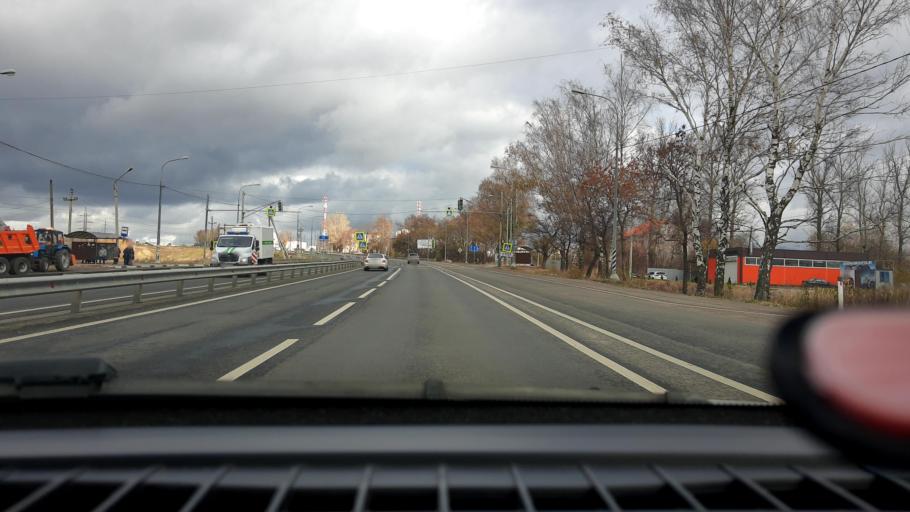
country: RU
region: Nizjnij Novgorod
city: Burevestnik
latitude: 56.1861
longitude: 43.9227
